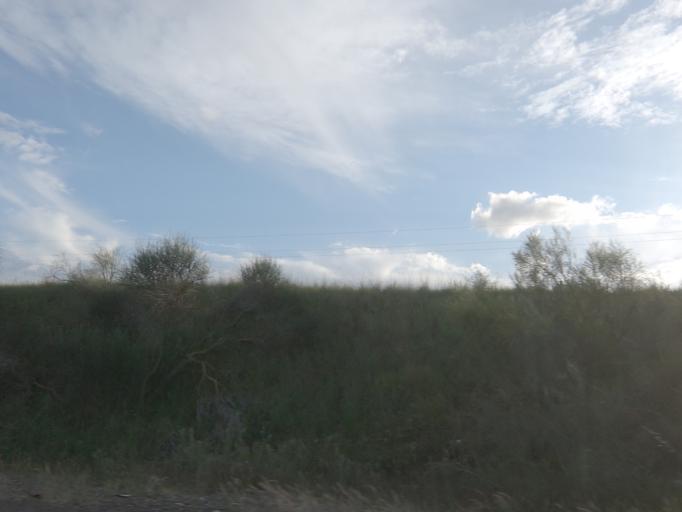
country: ES
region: Extremadura
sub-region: Provincia de Badajoz
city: Badajoz
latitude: 38.8820
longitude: -6.8890
